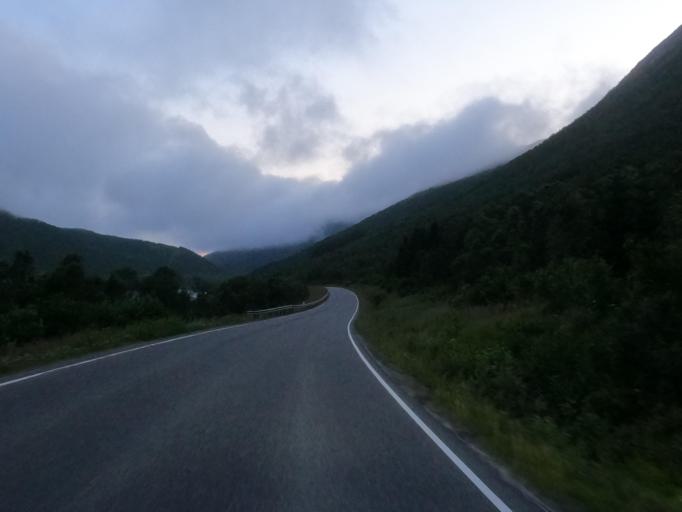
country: NO
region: Nordland
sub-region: Sortland
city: Sortland
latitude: 68.6194
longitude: 15.7143
